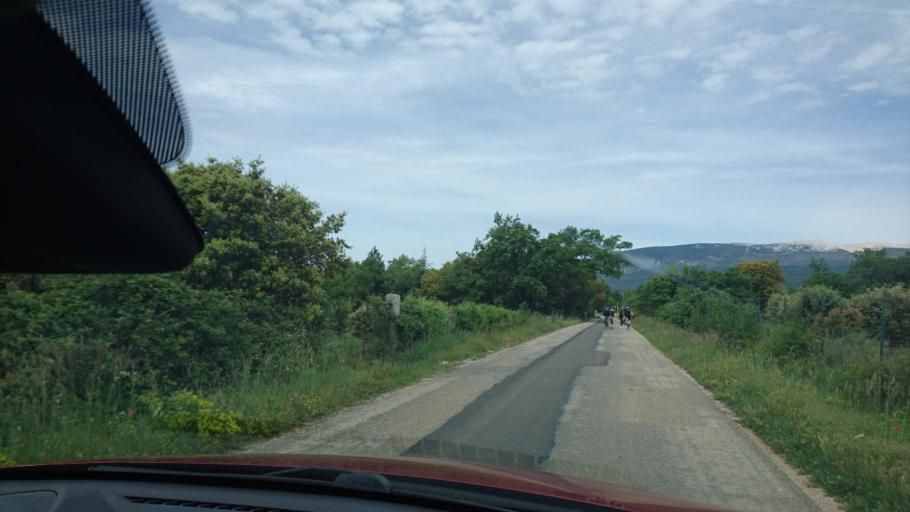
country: FR
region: Provence-Alpes-Cote d'Azur
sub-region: Departement du Vaucluse
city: Villes-sur-Auzon
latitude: 44.0799
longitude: 5.2351
